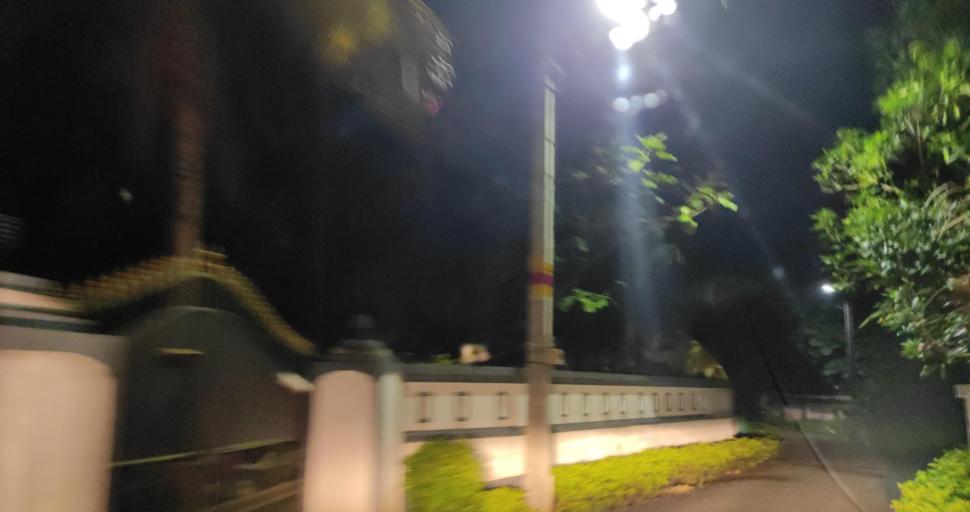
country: IN
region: Kerala
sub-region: Alappuzha
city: Shertallai
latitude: 9.6179
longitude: 76.3335
